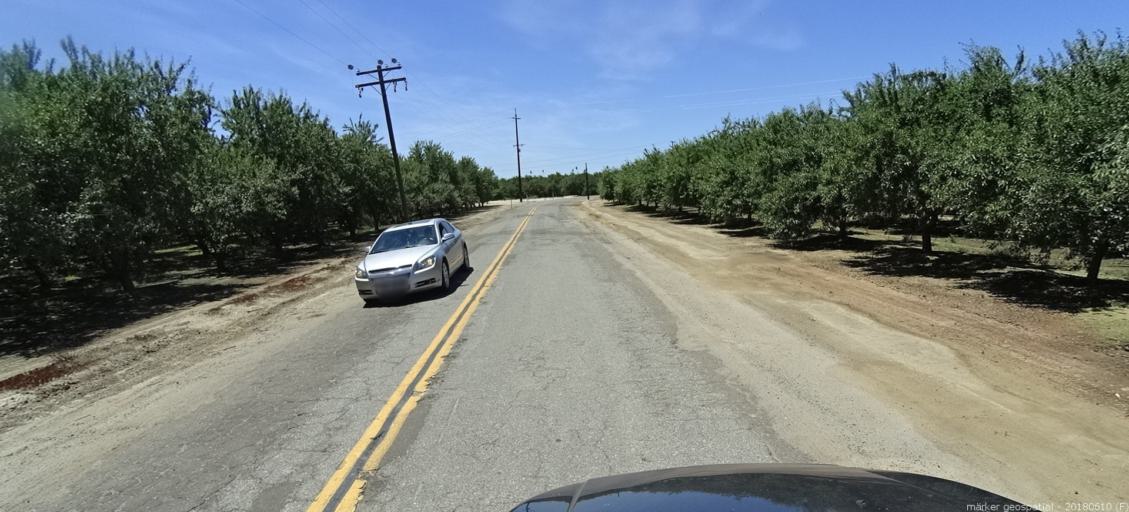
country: US
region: California
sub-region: Madera County
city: Chowchilla
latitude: 37.0617
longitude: -120.3088
